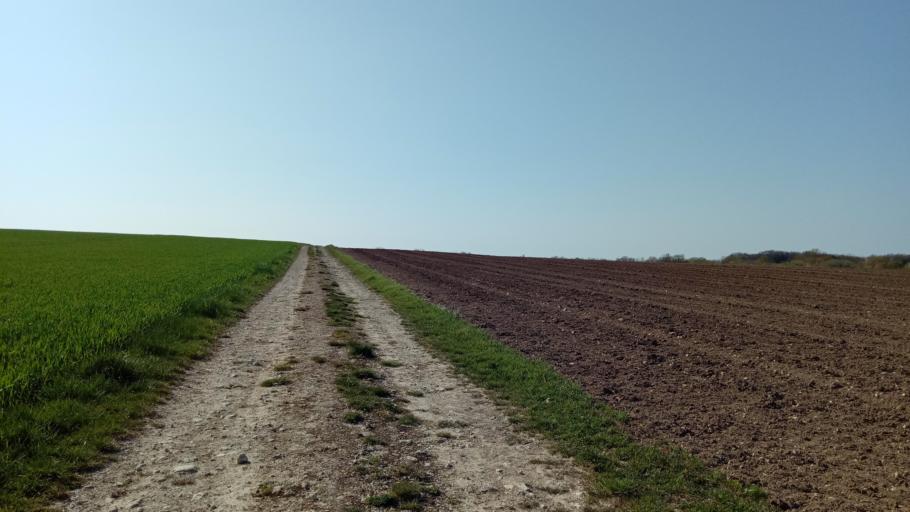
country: FR
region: Poitou-Charentes
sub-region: Departement de la Charente-Maritime
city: Verines
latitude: 46.1580
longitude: -0.9260
